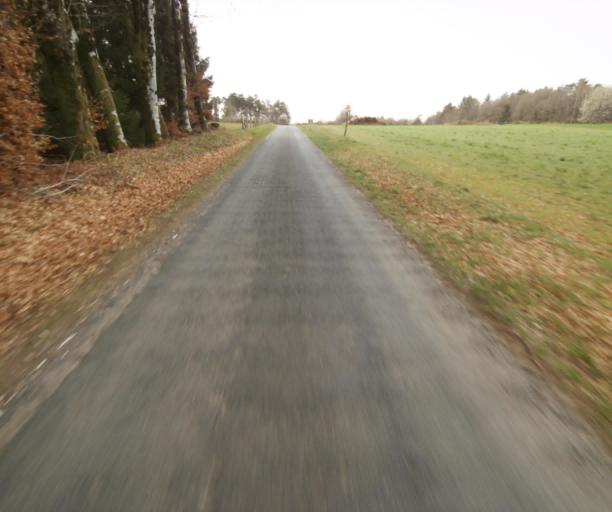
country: FR
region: Limousin
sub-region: Departement de la Correze
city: Correze
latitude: 45.4456
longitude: 1.8206
